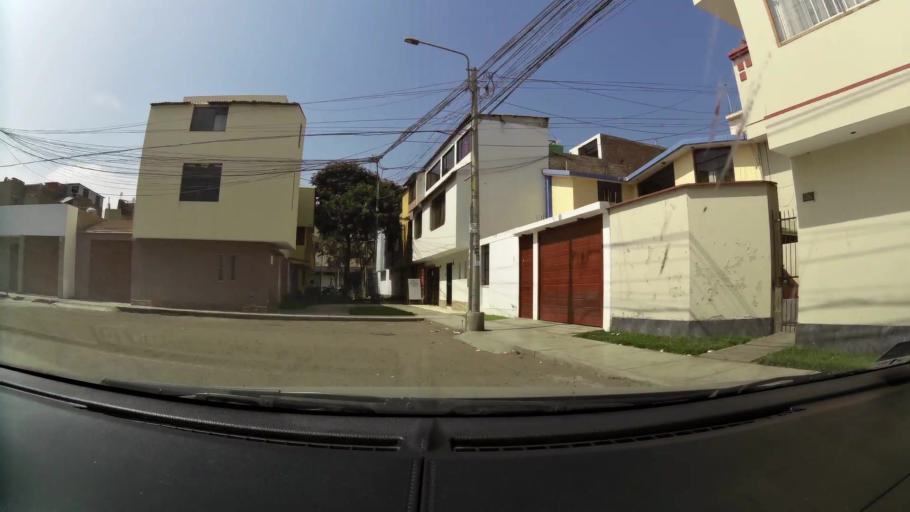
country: PE
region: La Libertad
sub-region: Provincia de Trujillo
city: Buenos Aires
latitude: -8.1268
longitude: -79.0414
